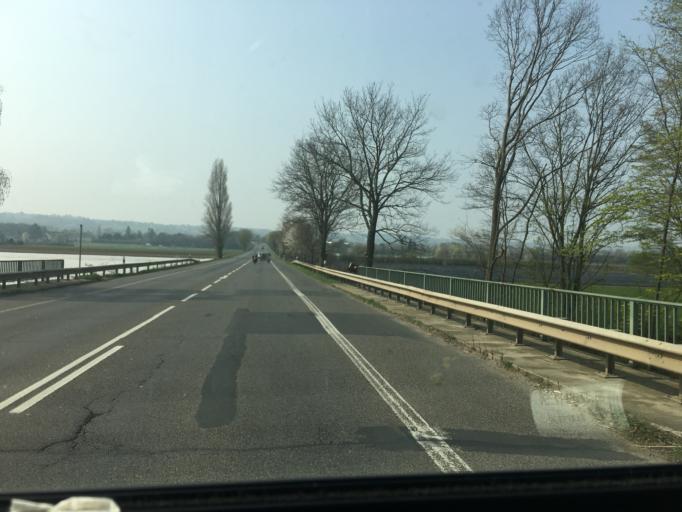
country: DE
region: North Rhine-Westphalia
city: Bornheim
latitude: 50.7735
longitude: 6.9841
